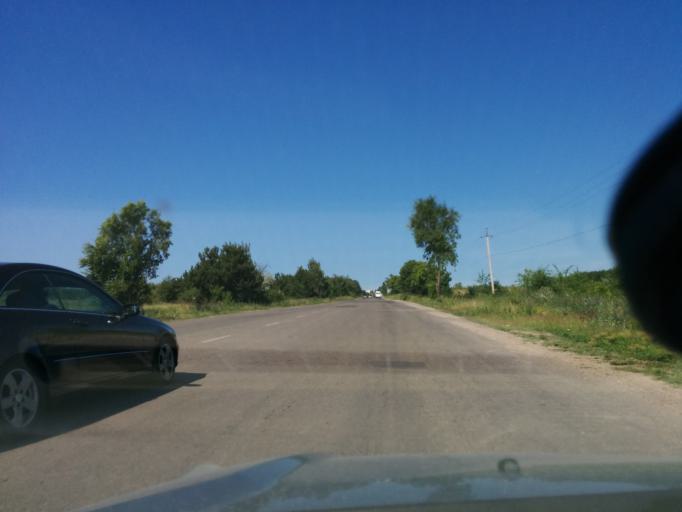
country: MD
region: Chisinau
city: Ciorescu
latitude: 47.0631
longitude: 28.9701
